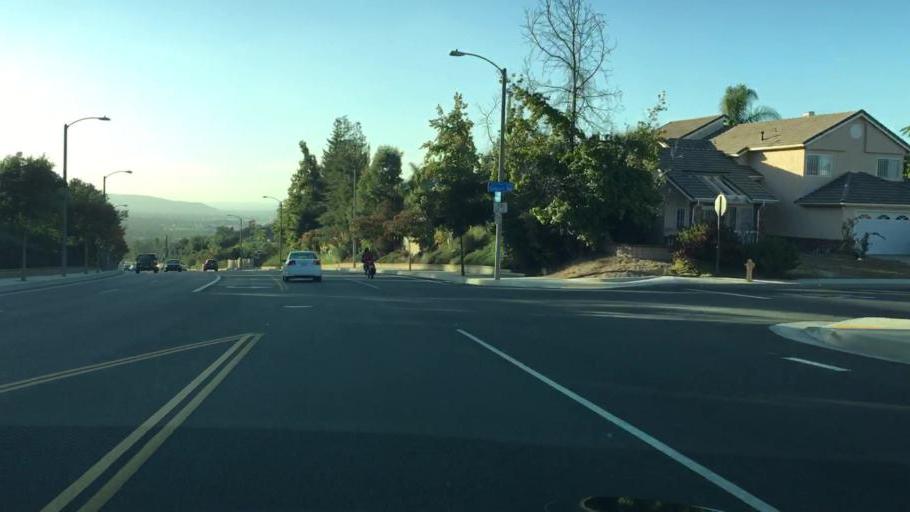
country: US
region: California
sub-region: Los Angeles County
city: Rowland Heights
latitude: 33.9721
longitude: -117.8689
